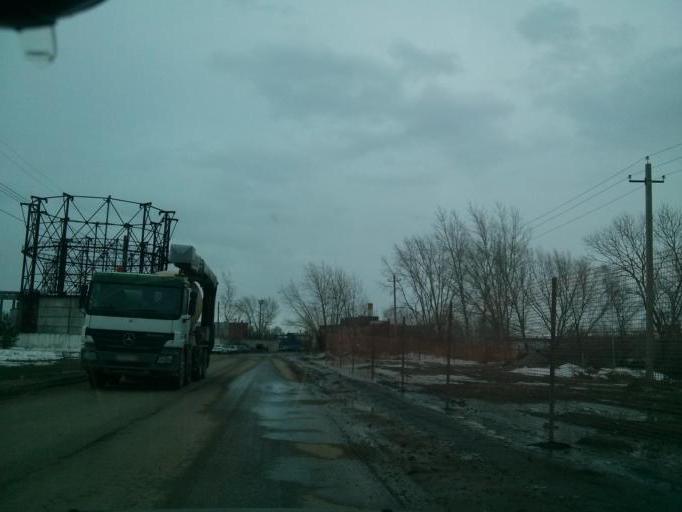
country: RU
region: Nizjnij Novgorod
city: Afonino
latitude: 56.2864
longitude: 44.1184
